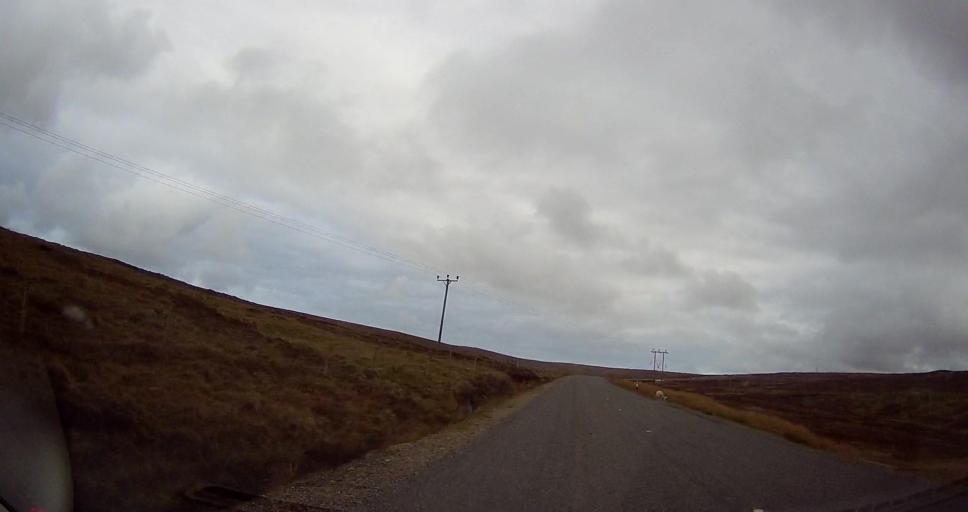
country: GB
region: Scotland
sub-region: Shetland Islands
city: Shetland
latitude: 60.6161
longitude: -1.0742
